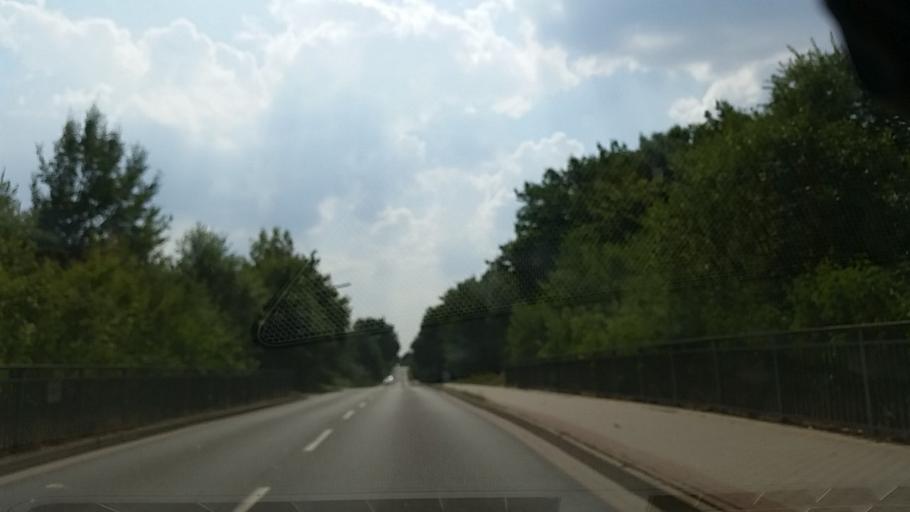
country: DE
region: Schleswig-Holstein
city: Ratzeburg
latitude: 53.6878
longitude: 10.7829
